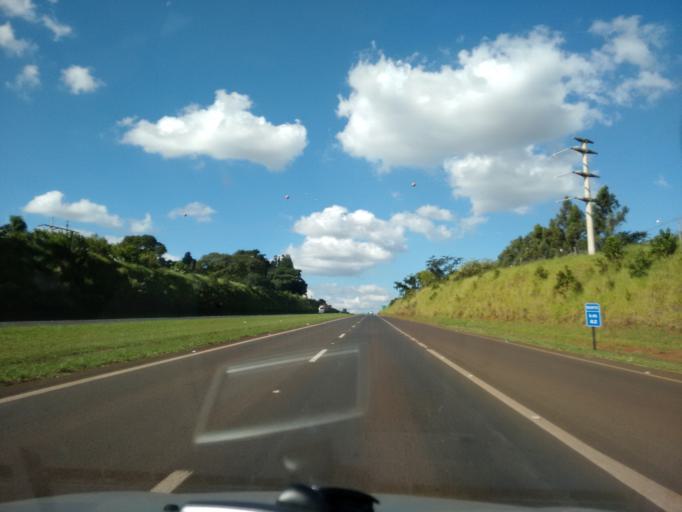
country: BR
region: Sao Paulo
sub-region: Araraquara
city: Araraquara
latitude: -21.8148
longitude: -48.1670
